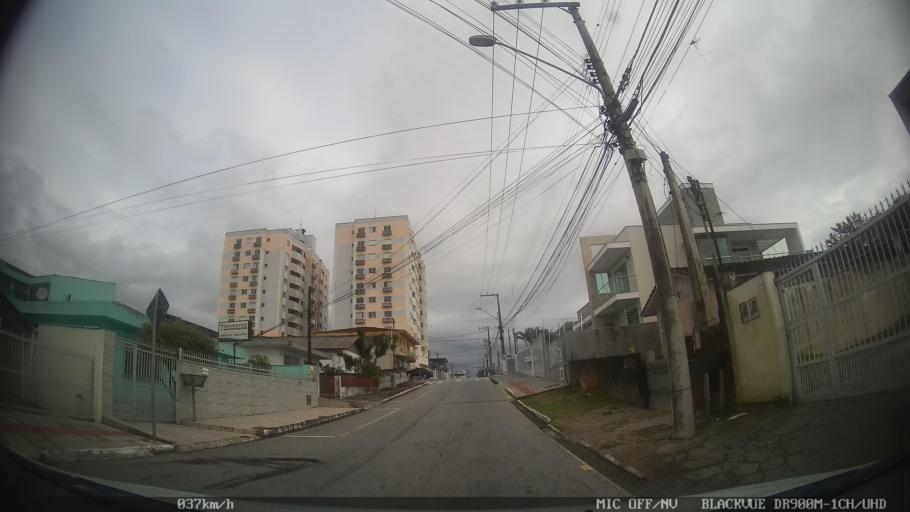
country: BR
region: Santa Catarina
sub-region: Sao Jose
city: Campinas
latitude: -27.5625
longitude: -48.6345
